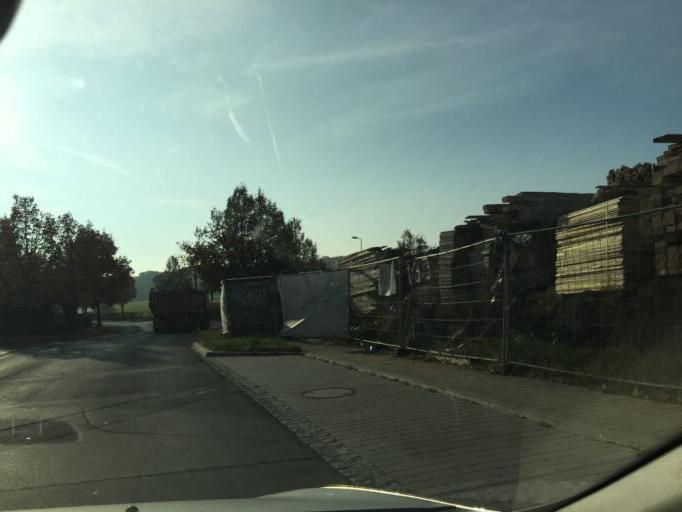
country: LU
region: Luxembourg
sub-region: Canton de Luxembourg
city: Contern
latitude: 49.5611
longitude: 6.2207
